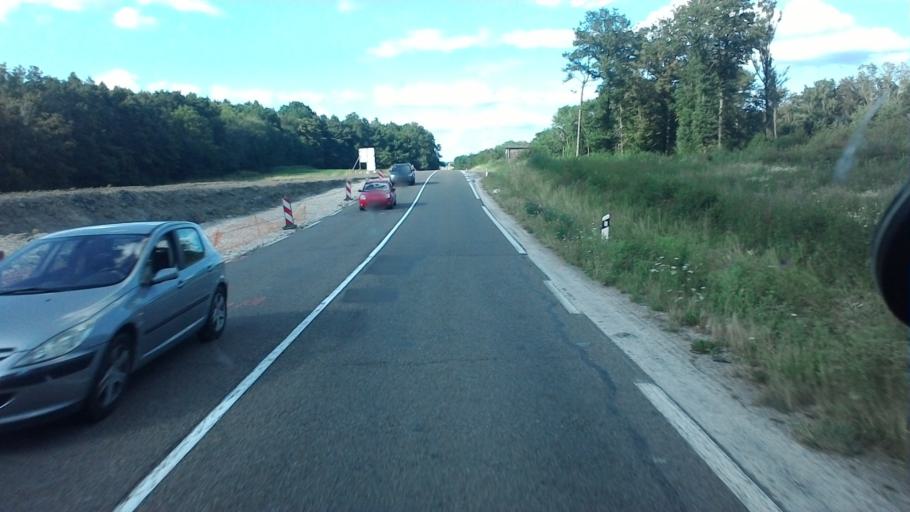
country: FR
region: Franche-Comte
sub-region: Departement de la Haute-Saone
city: Luxeuil-les-Bains
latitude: 47.7071
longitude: 6.2937
